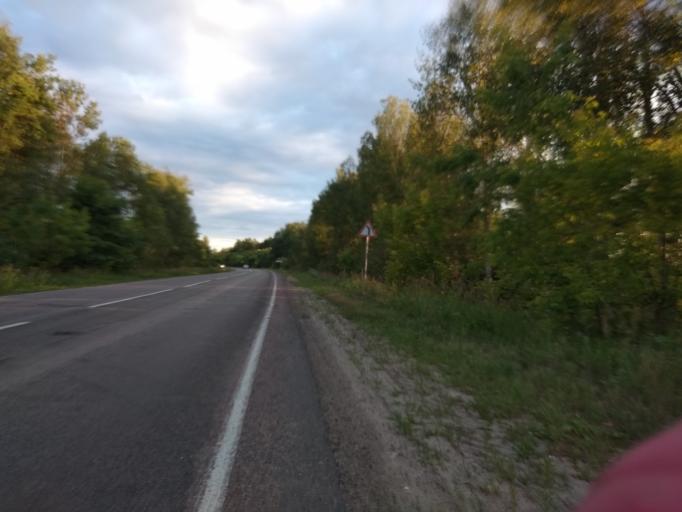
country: RU
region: Moskovskaya
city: Misheronskiy
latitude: 55.6060
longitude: 39.7103
